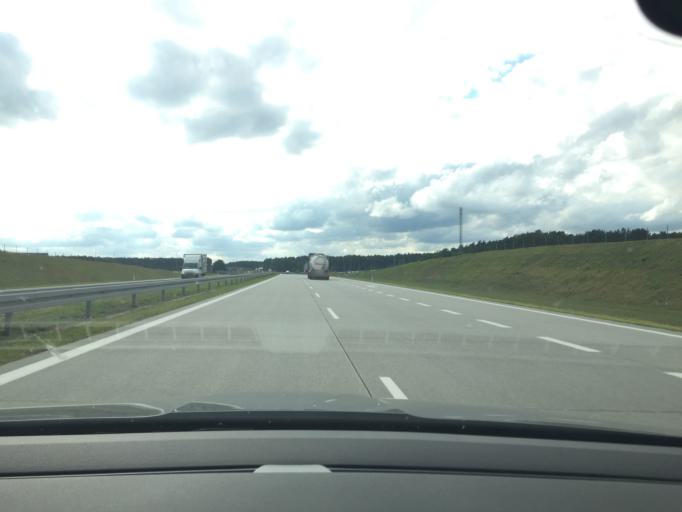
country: PL
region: Lubusz
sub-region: Powiat sulecinski
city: Torzym
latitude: 52.3248
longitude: 15.1705
